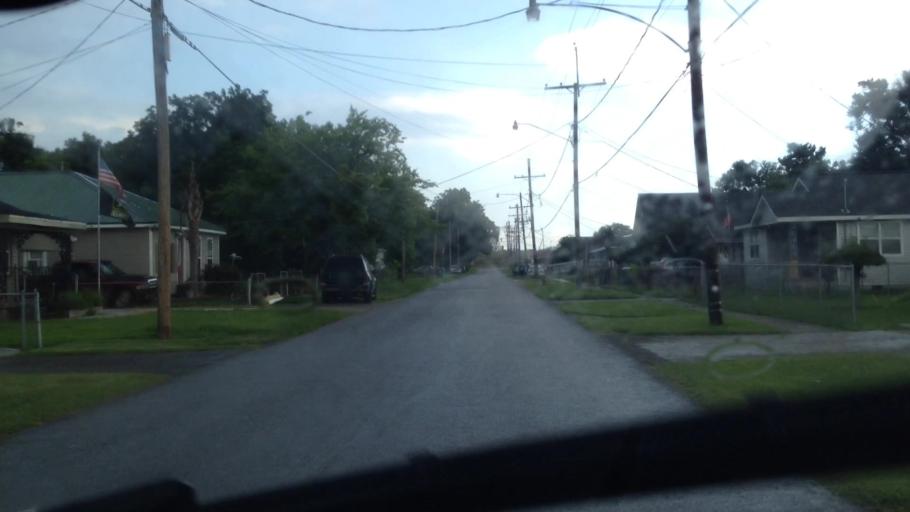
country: US
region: Louisiana
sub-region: Jefferson Parish
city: Bridge City
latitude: 29.9332
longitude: -90.1698
